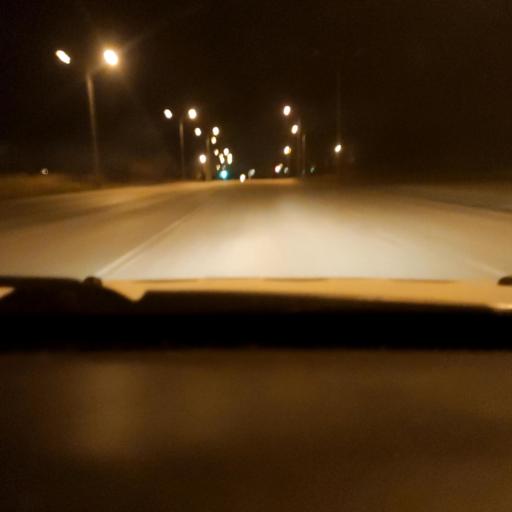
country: RU
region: Perm
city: Perm
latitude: 58.0997
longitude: 56.3879
